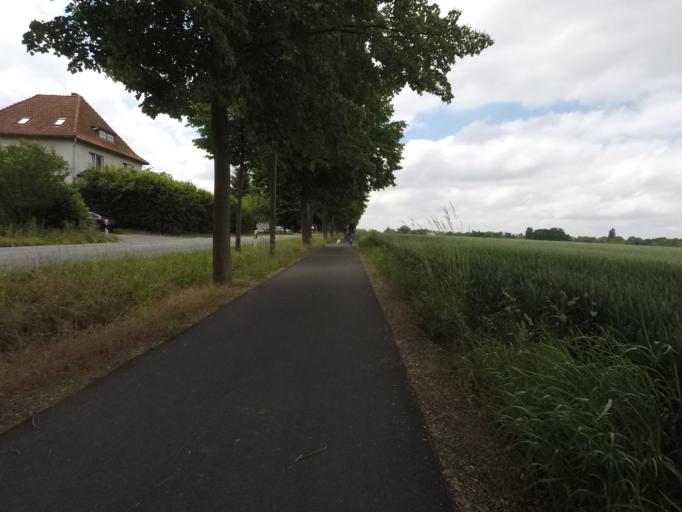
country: DE
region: North Rhine-Westphalia
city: Enger
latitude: 52.1321
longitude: 8.5279
